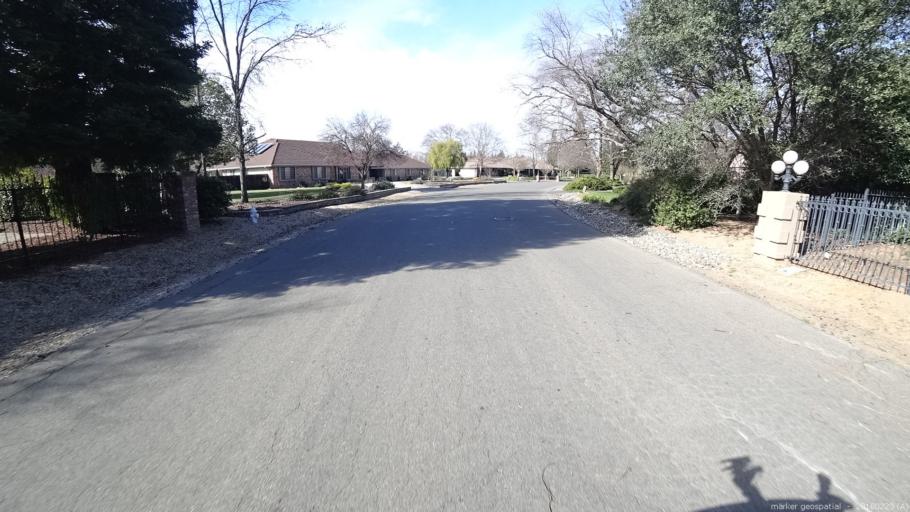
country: US
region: California
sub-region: Sacramento County
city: Orangevale
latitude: 38.7130
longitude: -121.2357
